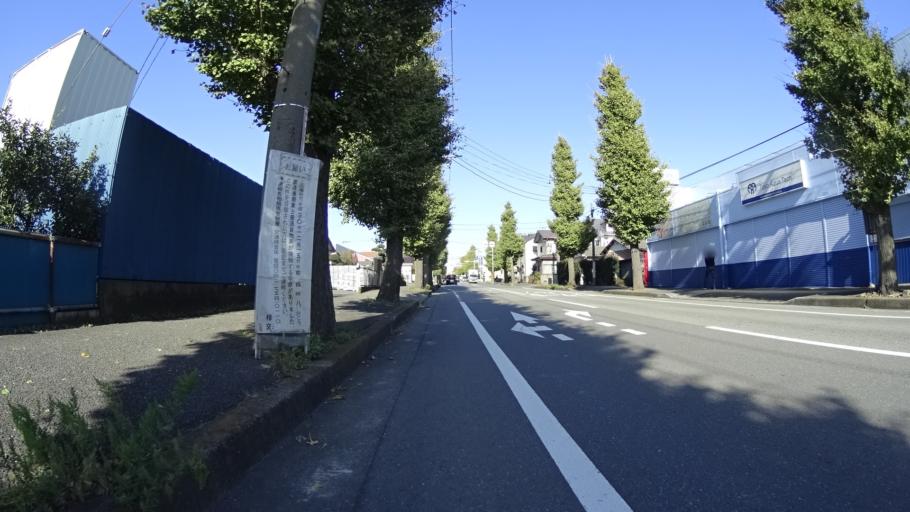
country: JP
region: Tokyo
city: Hachioji
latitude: 35.5738
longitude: 139.3597
